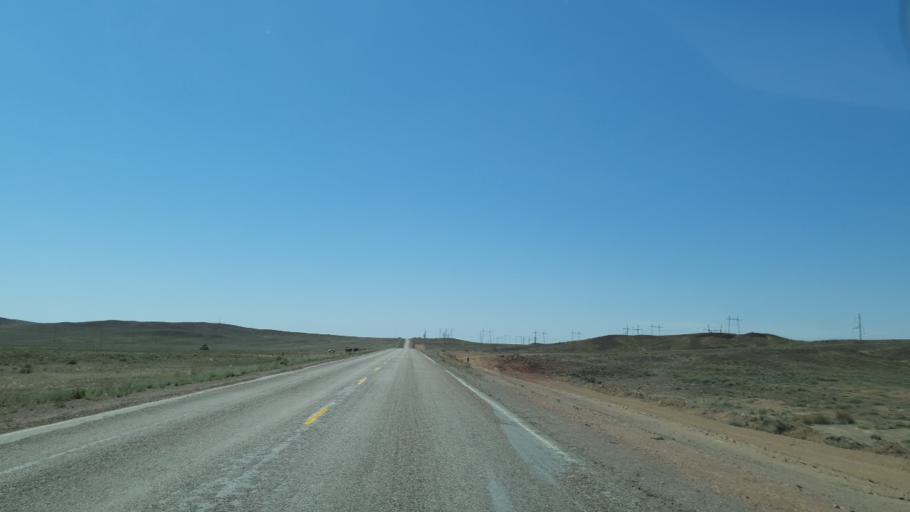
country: KZ
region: Zhambyl
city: Mynaral
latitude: 45.6792
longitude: 73.4010
